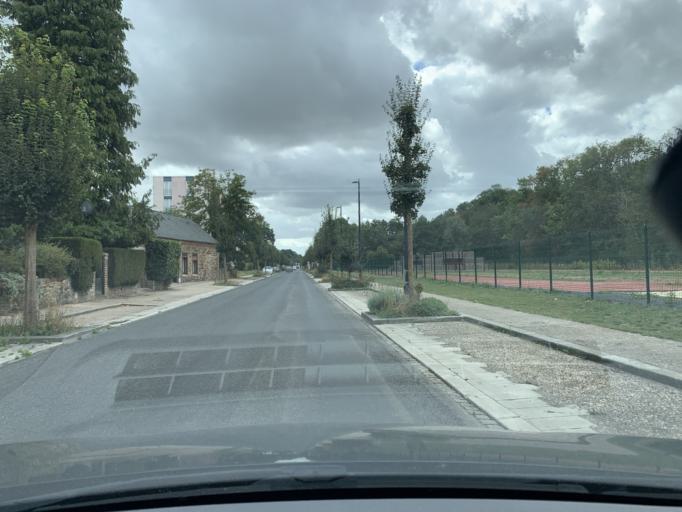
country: FR
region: Picardie
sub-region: Departement de l'Aisne
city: Saint-Michel
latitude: 49.9250
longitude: 4.1350
